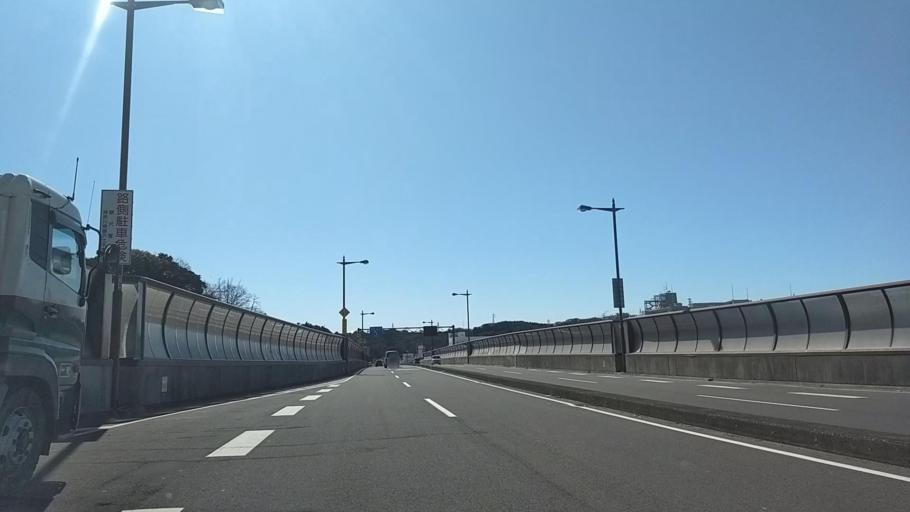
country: JP
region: Kanagawa
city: Fujisawa
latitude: 35.3383
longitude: 139.5026
